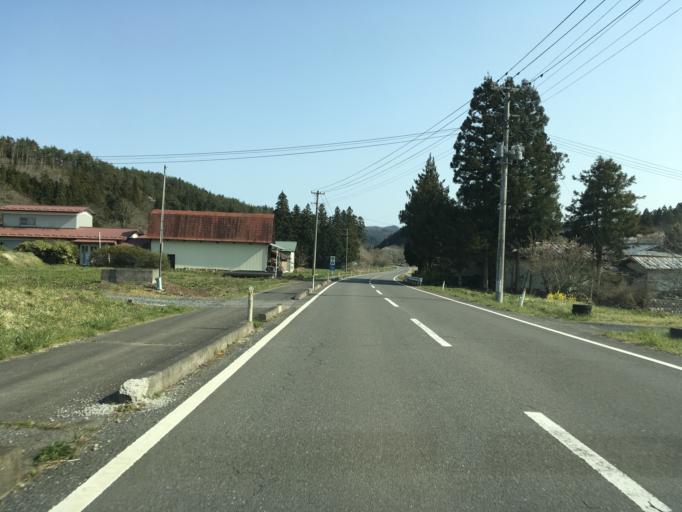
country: JP
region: Iwate
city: Ichinoseki
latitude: 38.7891
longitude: 141.3229
